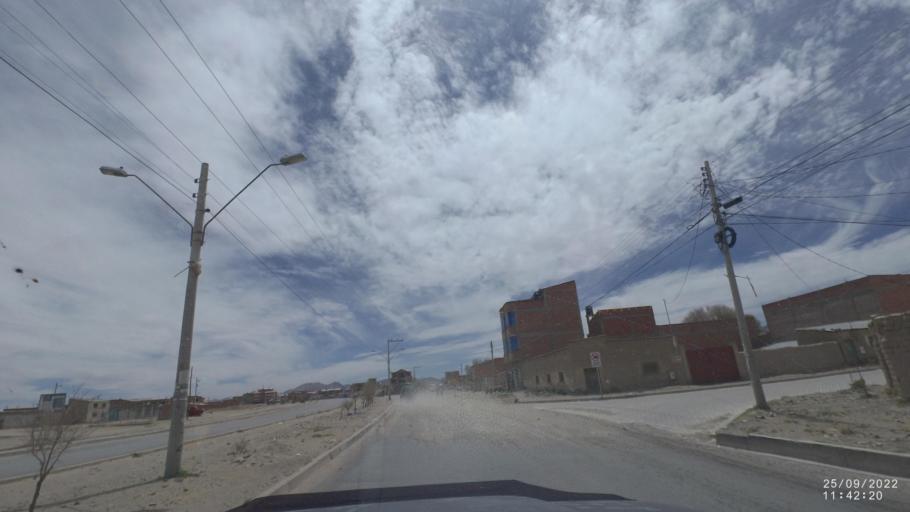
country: BO
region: Oruro
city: Challapata
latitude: -18.8978
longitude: -66.7765
